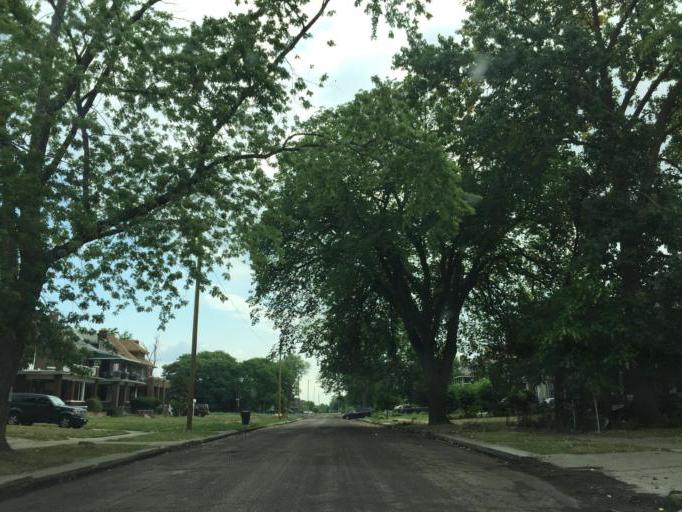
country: US
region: Michigan
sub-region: Wayne County
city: Highland Park
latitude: 42.3713
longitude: -83.0908
